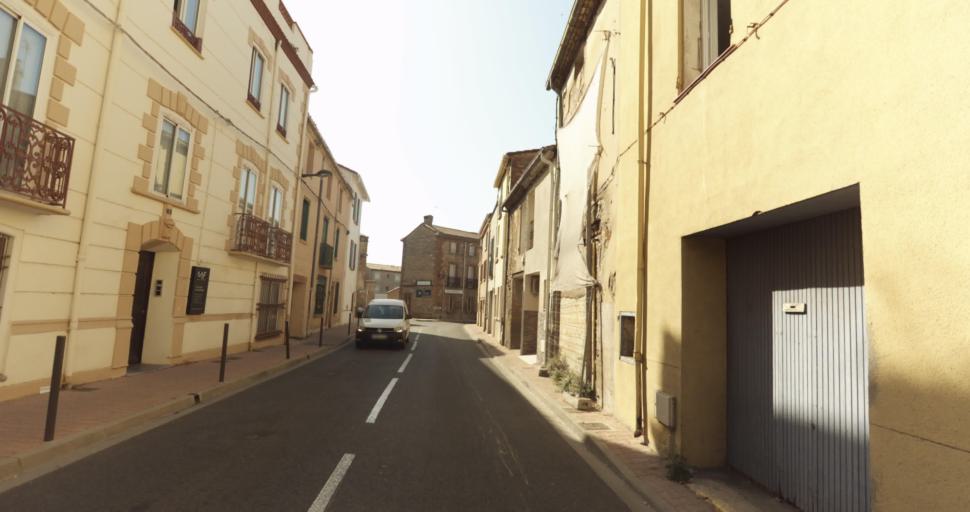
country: FR
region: Languedoc-Roussillon
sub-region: Departement des Pyrenees-Orientales
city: Alenya
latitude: 42.6382
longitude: 2.9811
